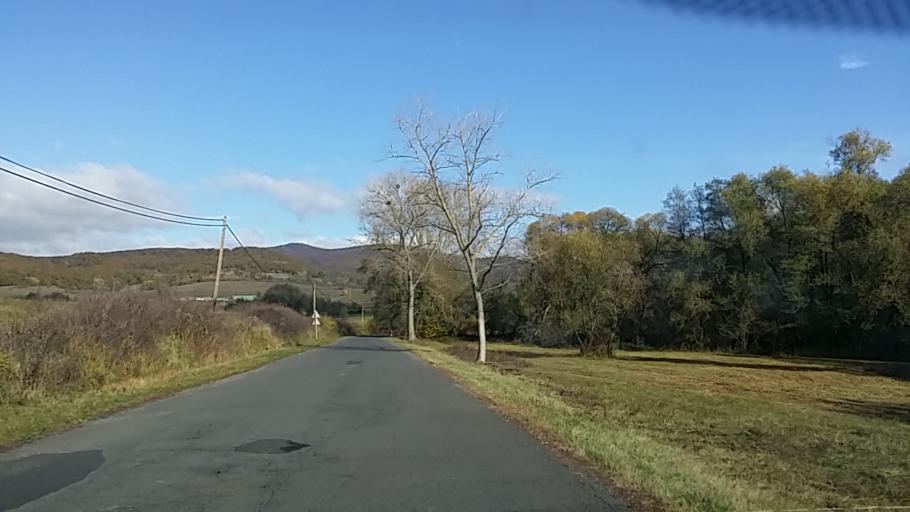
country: HU
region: Borsod-Abauj-Zemplen
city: Gonc
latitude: 48.3860
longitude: 21.3301
